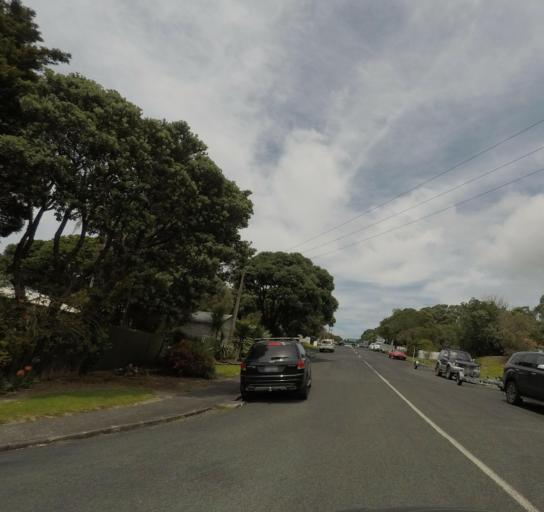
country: NZ
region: Auckland
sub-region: Auckland
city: Warkworth
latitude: -36.2895
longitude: 174.8049
